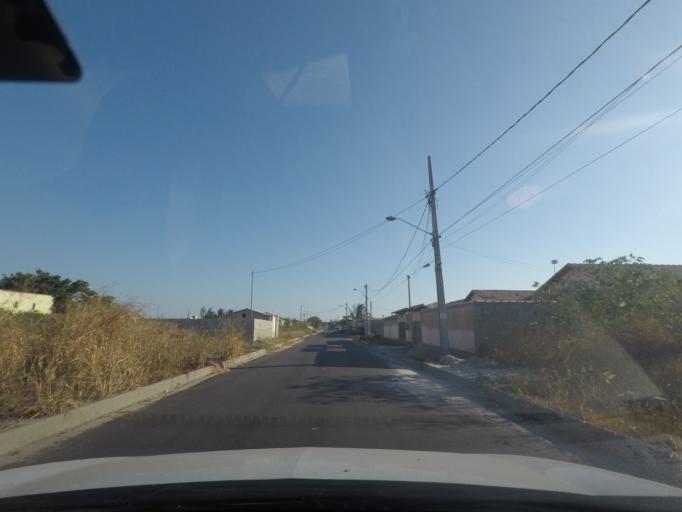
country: BR
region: Rio de Janeiro
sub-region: Marica
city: Marica
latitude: -22.9605
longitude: -42.9378
